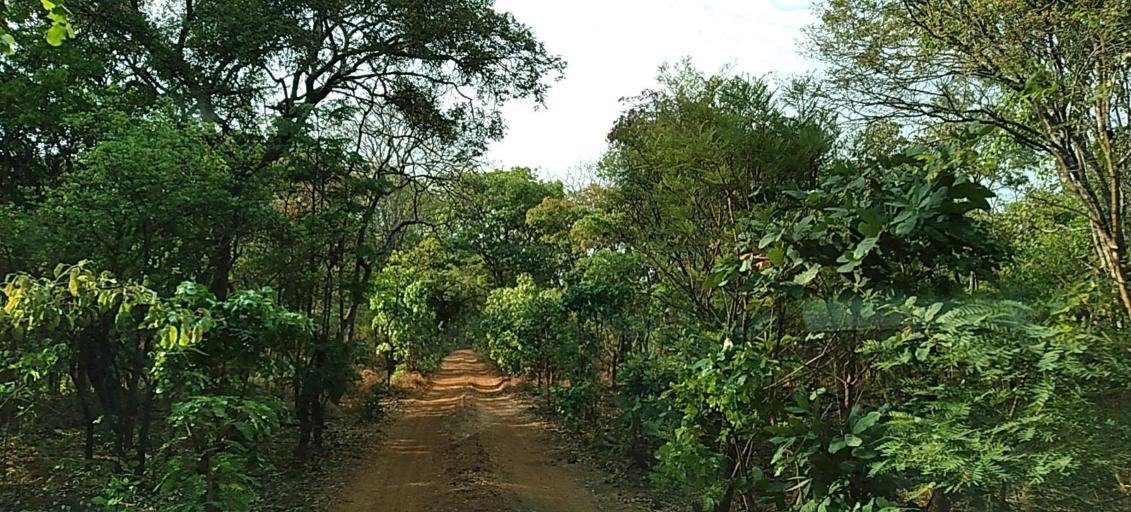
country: ZM
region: Copperbelt
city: Kalulushi
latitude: -12.9830
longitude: 27.7187
